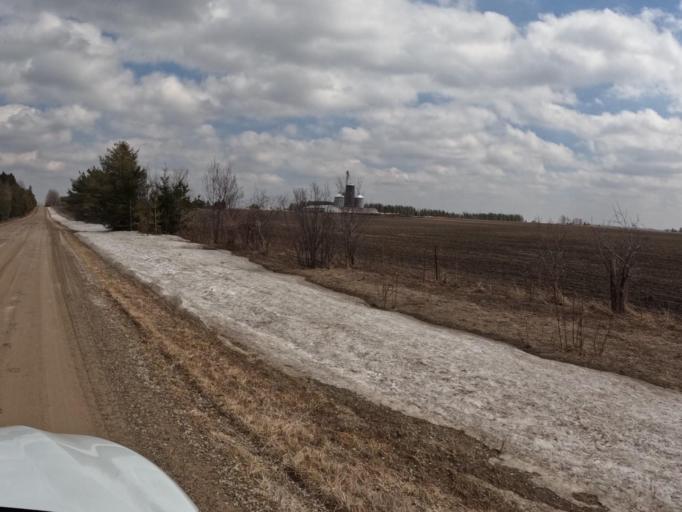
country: CA
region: Ontario
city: Shelburne
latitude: 44.0289
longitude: -80.2483
